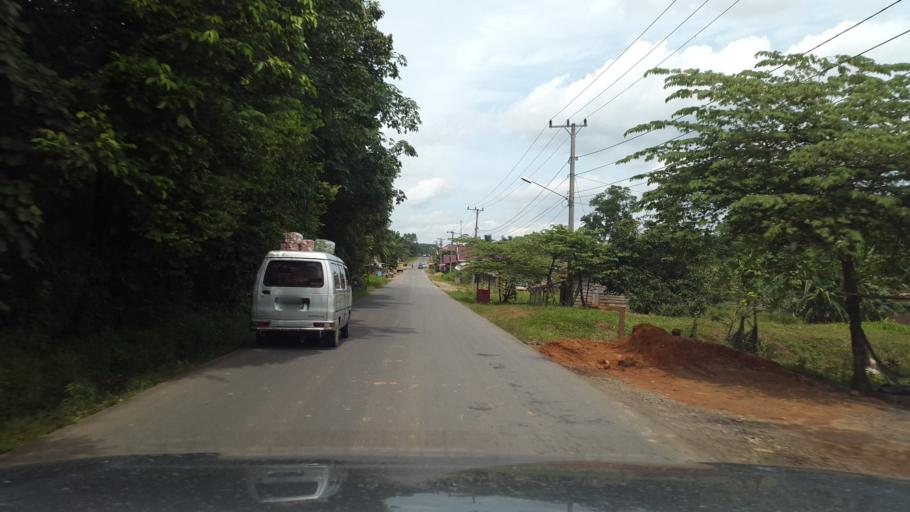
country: ID
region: South Sumatra
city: Gunungmegang Dalam
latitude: -3.3408
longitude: 103.9129
